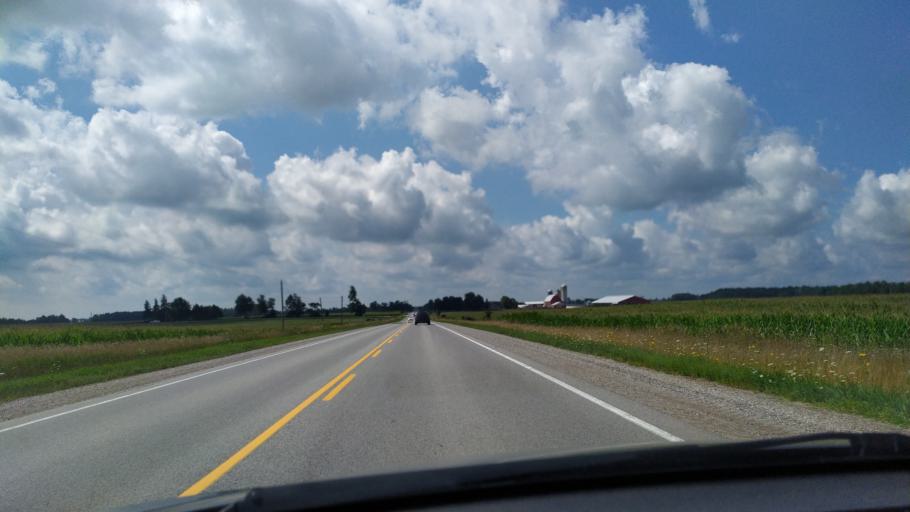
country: CA
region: Ontario
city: South Huron
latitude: 43.2962
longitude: -81.3368
